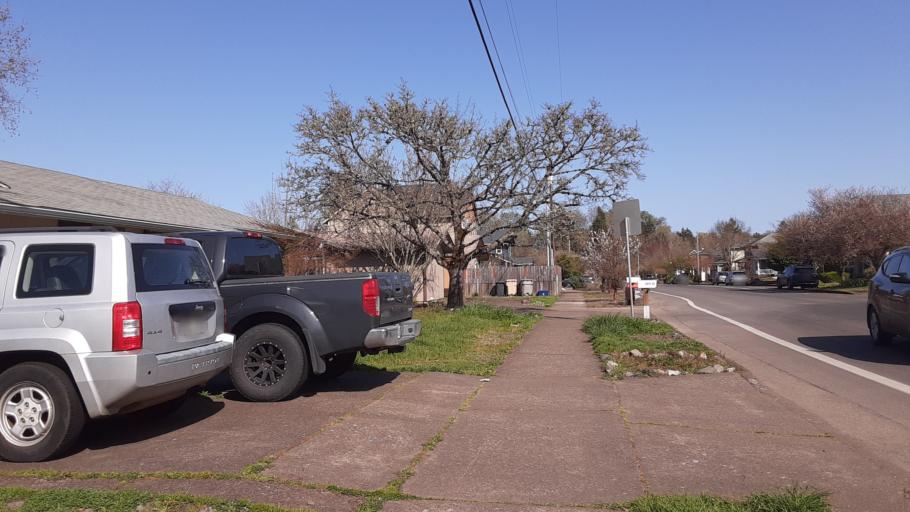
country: US
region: Oregon
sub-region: Benton County
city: Corvallis
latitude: 44.5369
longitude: -123.2571
